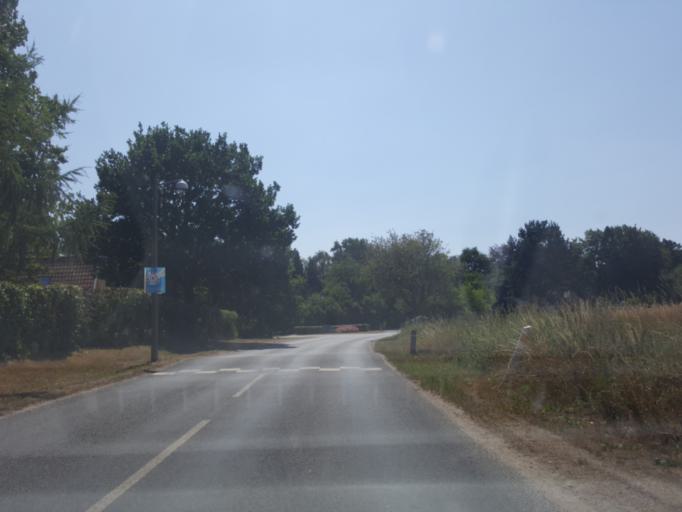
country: DK
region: Capital Region
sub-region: Fredensborg Kommune
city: Kokkedal
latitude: 55.9300
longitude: 12.4684
